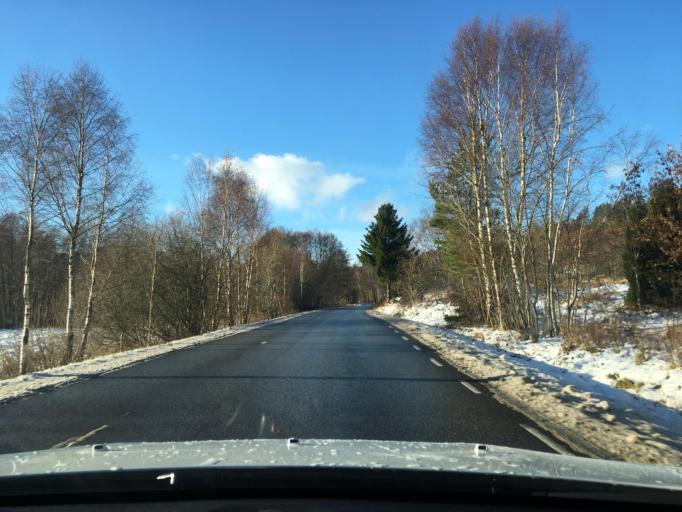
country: SE
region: Vaestra Goetaland
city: Svanesund
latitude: 58.1388
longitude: 11.7775
